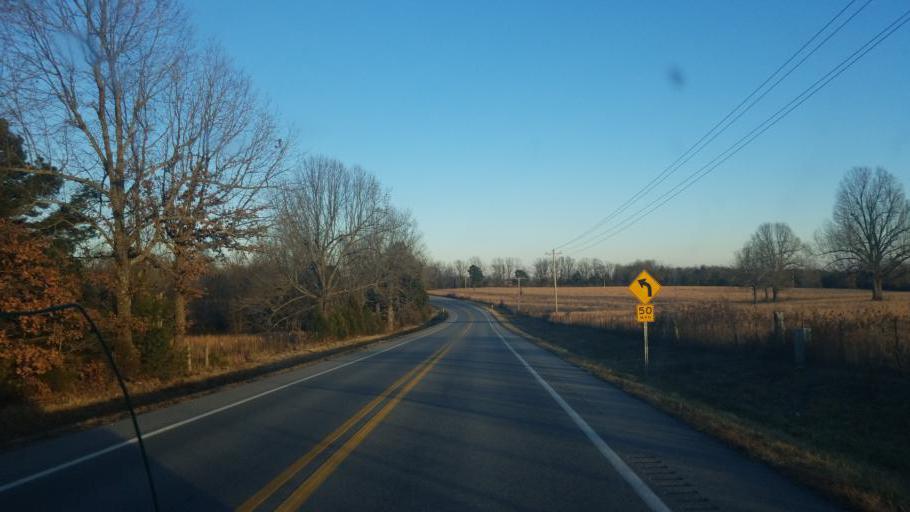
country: US
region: Arkansas
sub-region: Baxter County
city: Mountain Home
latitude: 36.3756
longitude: -92.1406
